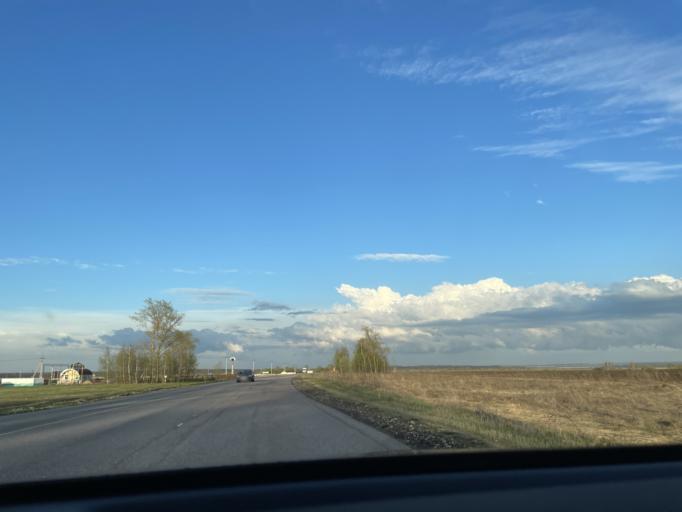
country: RU
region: Tula
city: Novogurovskiy
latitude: 54.5295
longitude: 37.3855
